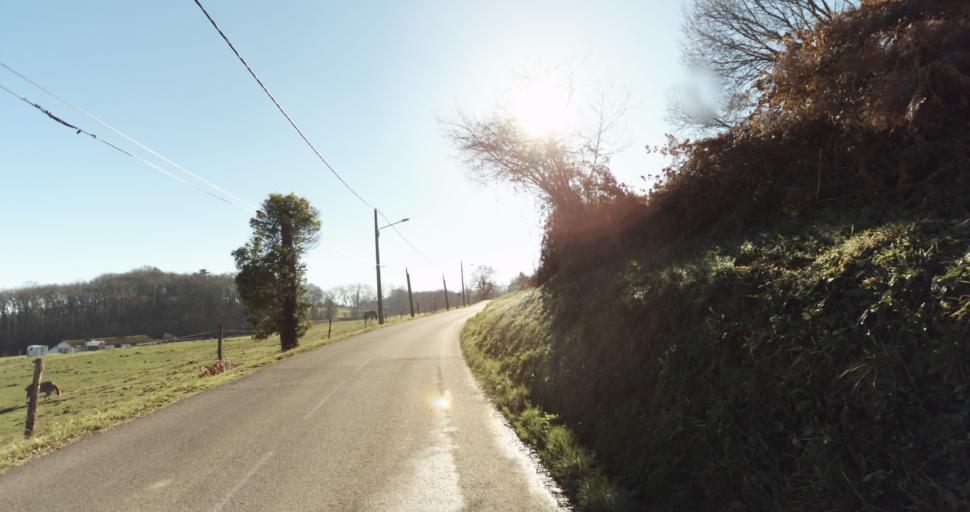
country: FR
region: Aquitaine
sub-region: Departement des Pyrenees-Atlantiques
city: Morlaas
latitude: 43.3579
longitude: -0.2653
